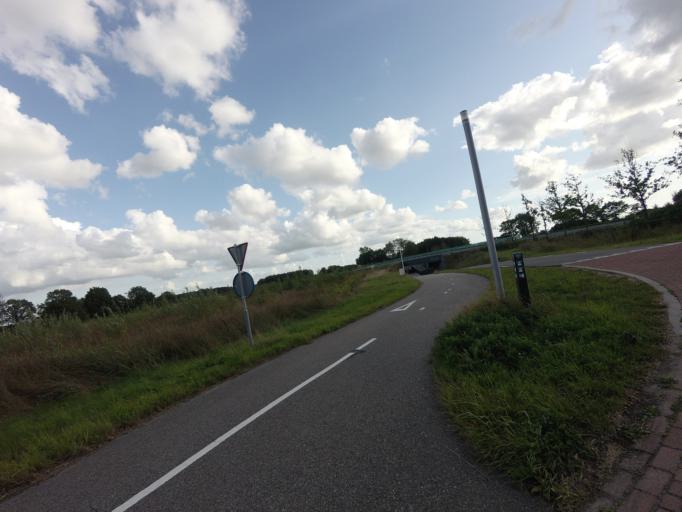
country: NL
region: Friesland
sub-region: Gemeente Heerenveen
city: Jubbega
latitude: 53.0010
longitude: 6.2314
